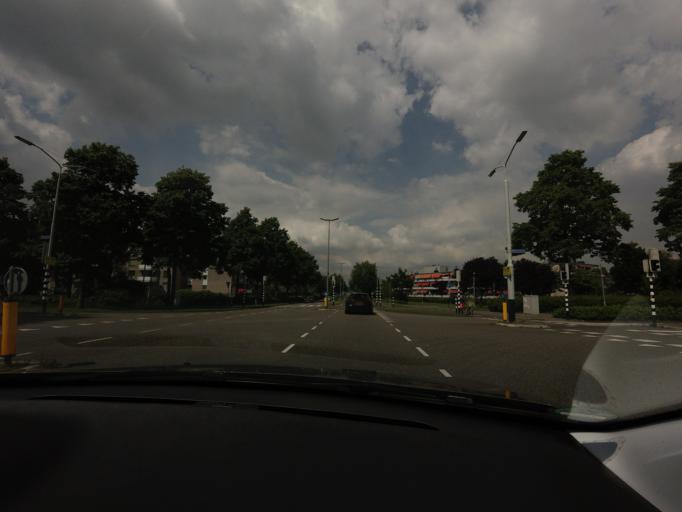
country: NL
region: South Holland
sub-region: Gemeente Barendrecht
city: Barendrecht
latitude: 51.8462
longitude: 4.5363
